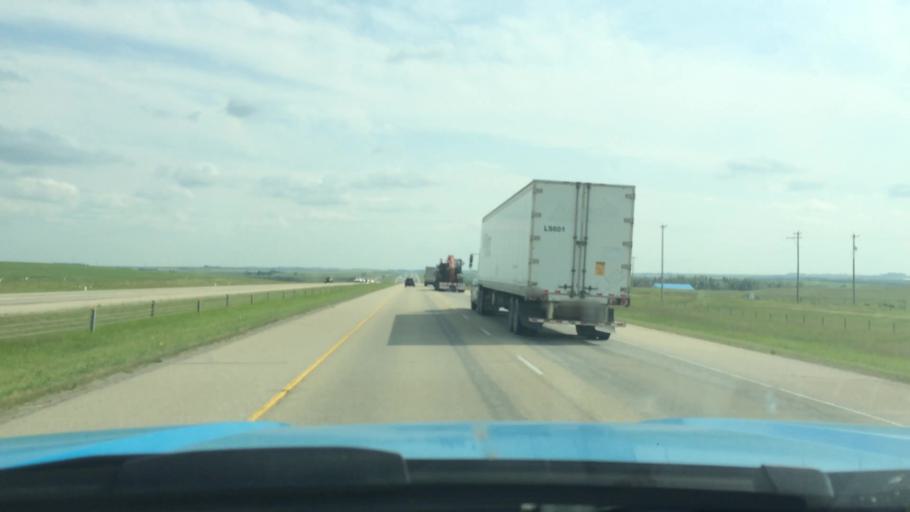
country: CA
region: Alberta
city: Carstairs
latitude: 51.5269
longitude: -114.0252
